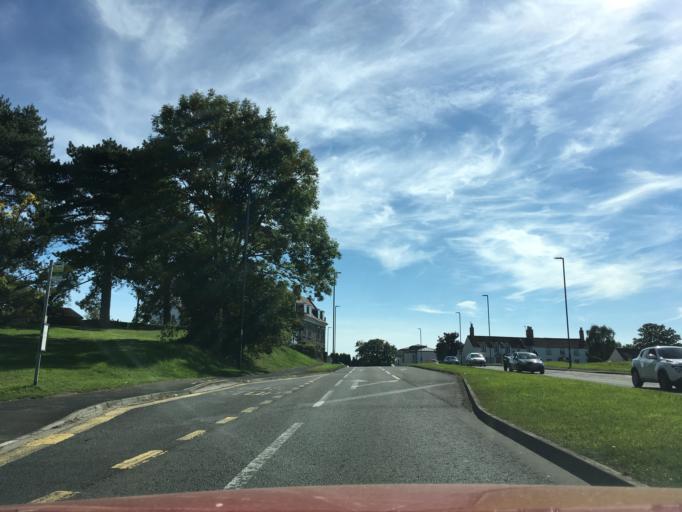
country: GB
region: England
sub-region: South Gloucestershire
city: Almondsbury
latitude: 51.5530
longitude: -2.5692
